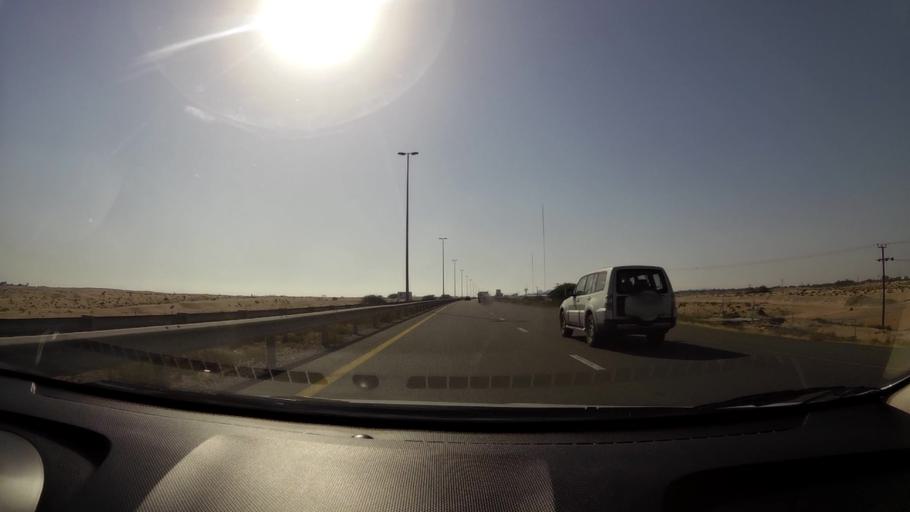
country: AE
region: Umm al Qaywayn
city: Umm al Qaywayn
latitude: 25.4781
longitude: 55.5677
